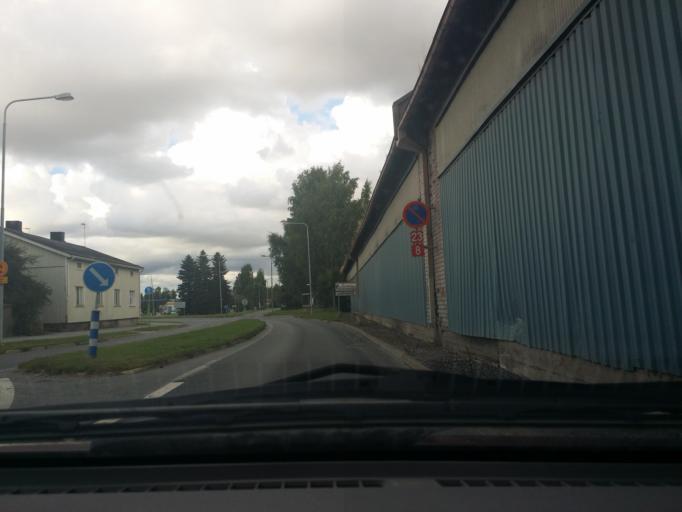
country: FI
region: Satakunta
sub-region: Pori
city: Pori
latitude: 61.4955
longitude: 21.8049
